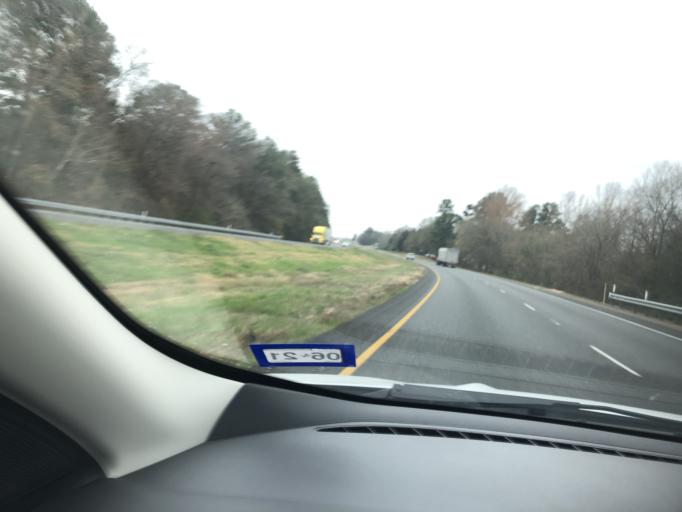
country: US
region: Texas
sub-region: Angelina County
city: Redland
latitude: 31.4757
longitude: -94.7262
